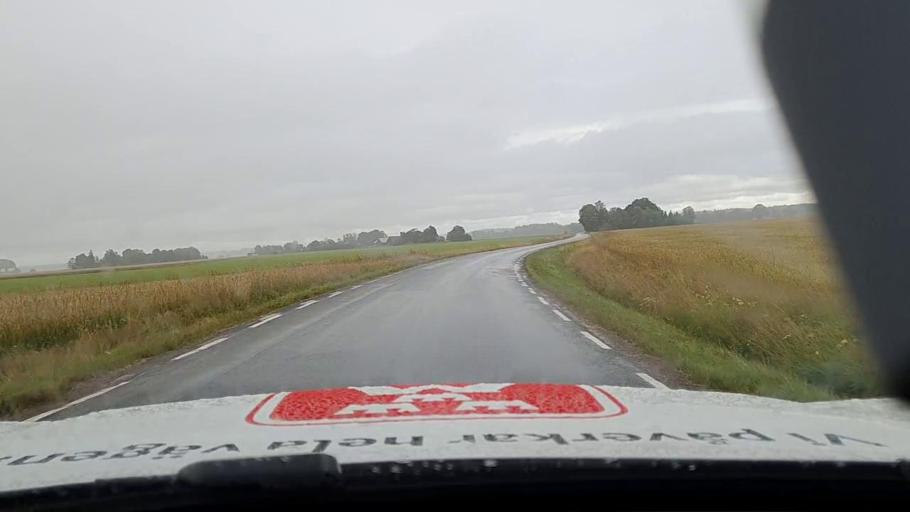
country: SE
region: Vaestra Goetaland
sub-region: Toreboda Kommun
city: Toereboda
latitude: 58.6543
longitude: 14.1083
